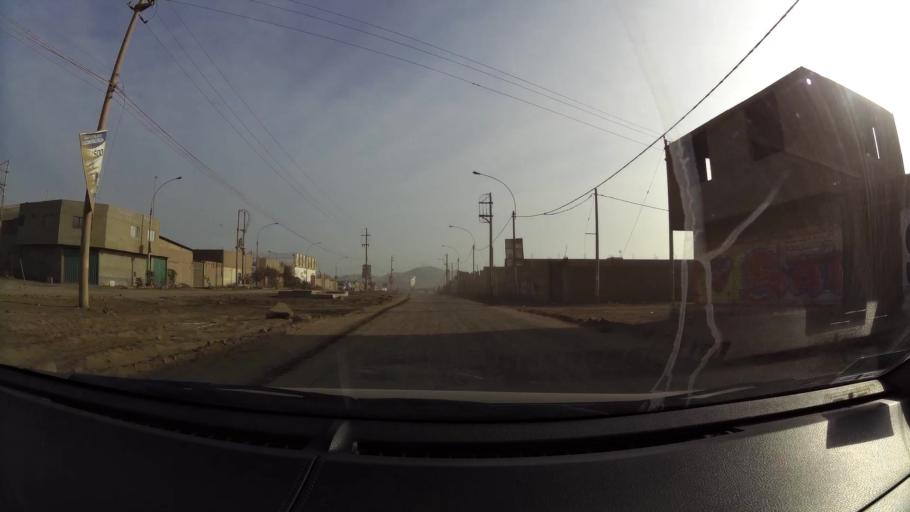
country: PE
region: Lima
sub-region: Lima
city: Santa Rosa
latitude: -11.7604
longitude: -77.1592
